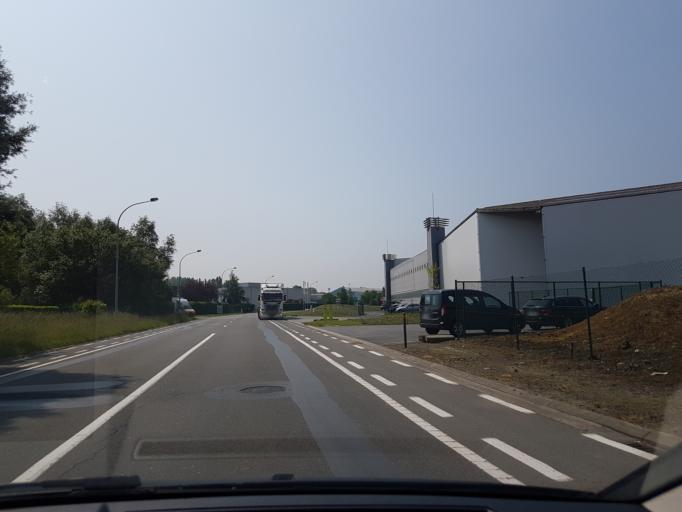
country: BE
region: Flanders
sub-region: Provincie Oost-Vlaanderen
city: Aalst
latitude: 50.9632
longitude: 4.0467
